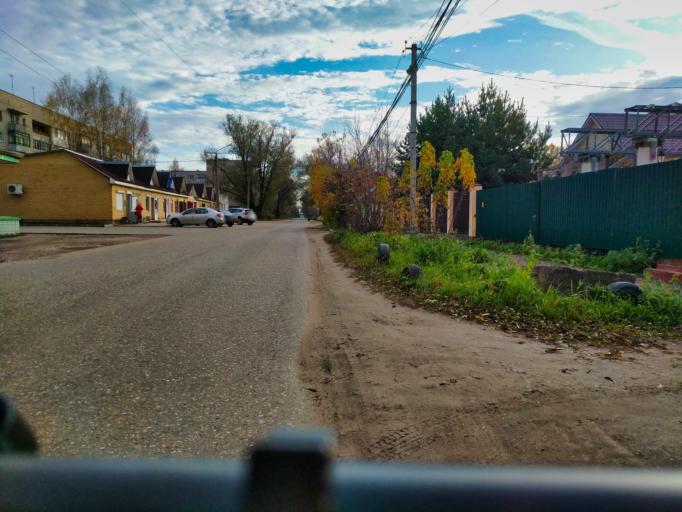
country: RU
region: Tverskaya
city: Rzhev
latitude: 56.2490
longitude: 34.3308
